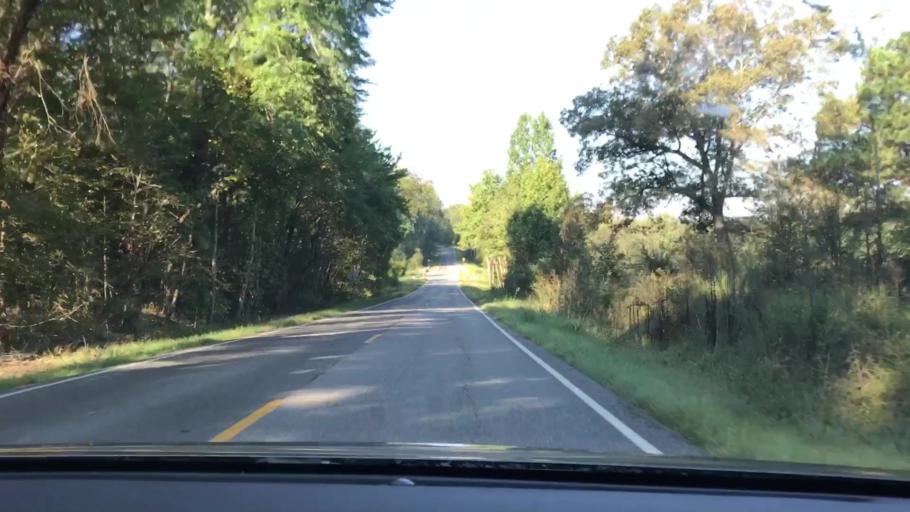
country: US
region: Kentucky
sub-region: Marshall County
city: Benton
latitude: 36.7668
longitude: -88.1852
